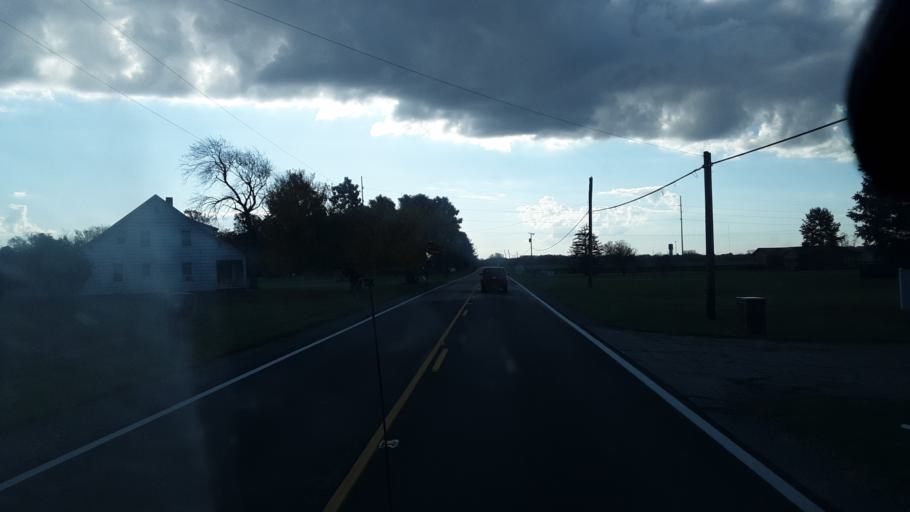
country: US
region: Ohio
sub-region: Fayette County
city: Washington Court House
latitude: 39.5663
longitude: -83.4624
